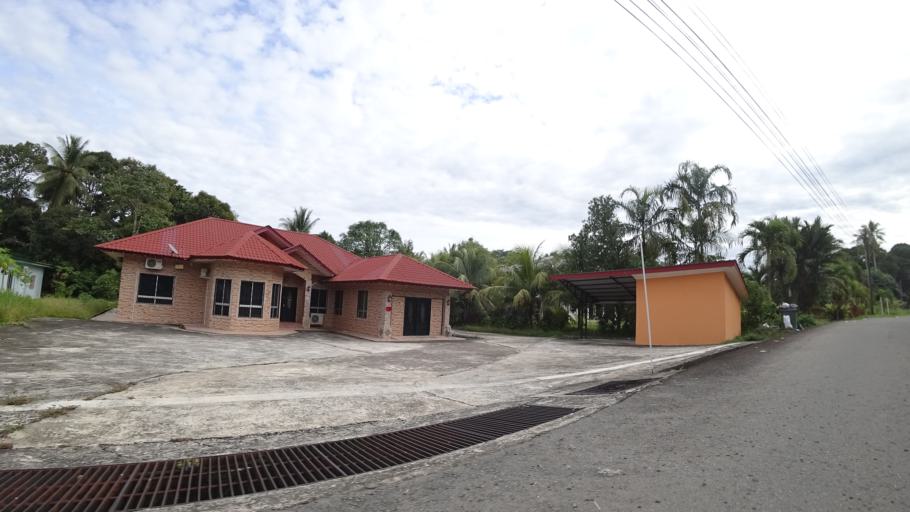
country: MY
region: Sarawak
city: Limbang
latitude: 4.8177
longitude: 114.9458
